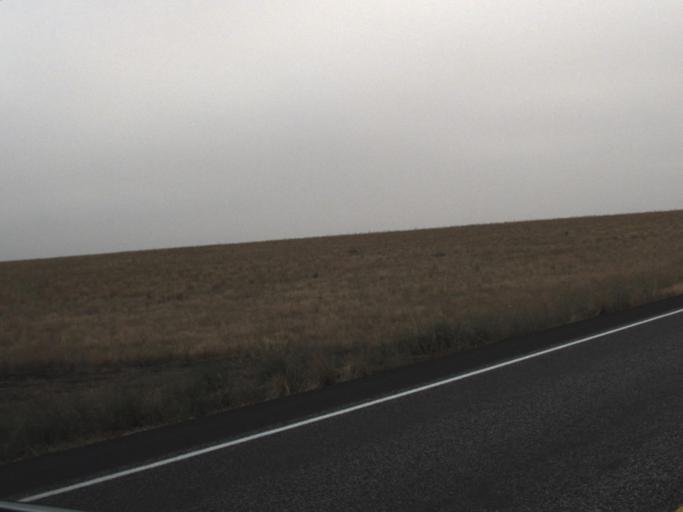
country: US
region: Washington
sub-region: Benton County
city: Prosser
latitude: 46.1873
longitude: -119.6793
